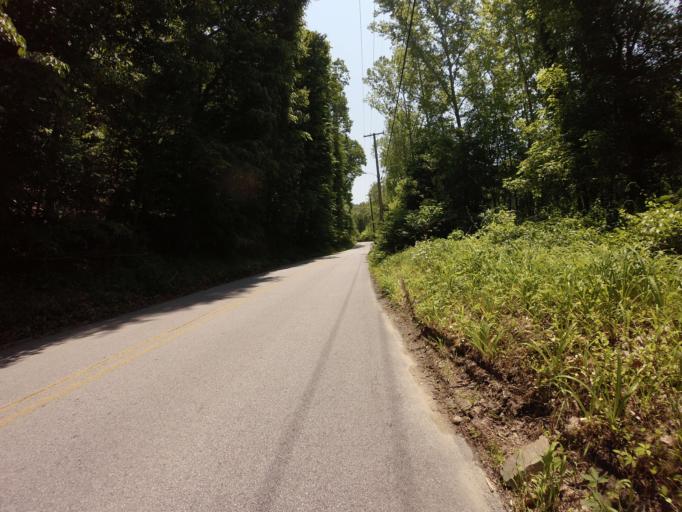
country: US
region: Maryland
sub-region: Howard County
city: Ellicott City
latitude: 39.2589
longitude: -76.7817
